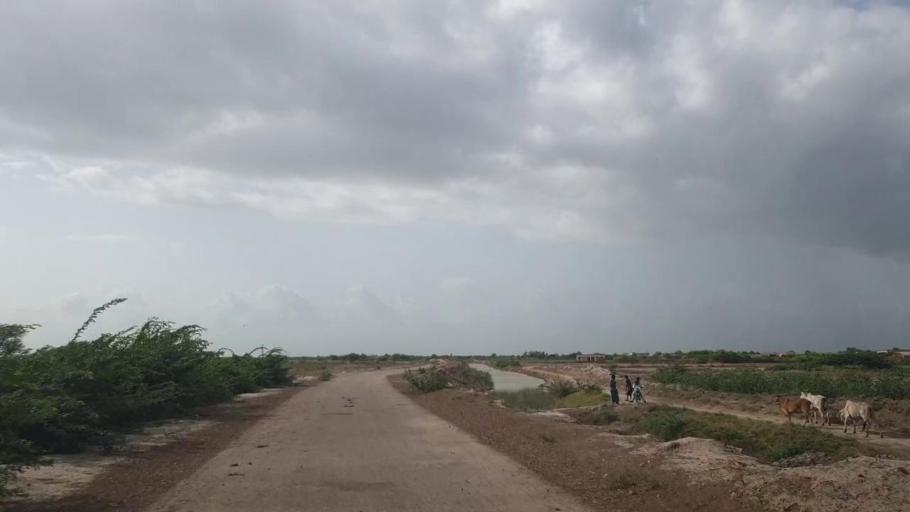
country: PK
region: Sindh
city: Kadhan
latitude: 24.5672
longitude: 69.0629
